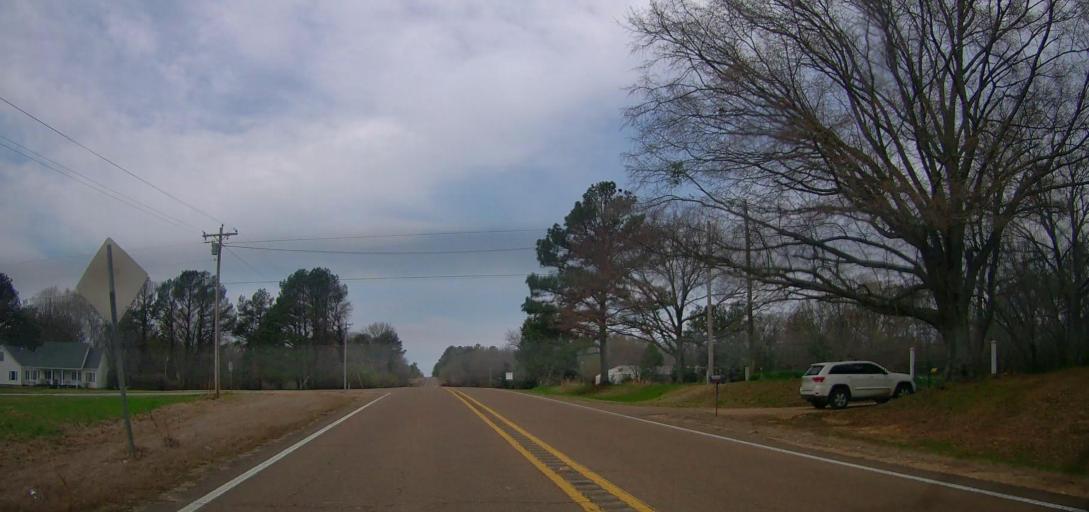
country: US
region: Mississippi
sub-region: Marshall County
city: Byhalia
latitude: 34.8368
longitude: -89.5902
